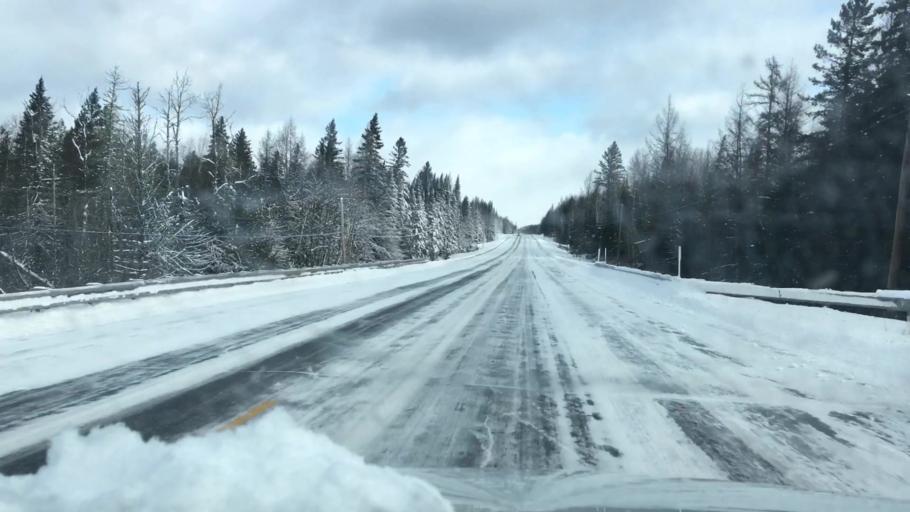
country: US
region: Maine
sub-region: Aroostook County
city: Madawaska
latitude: 47.0214
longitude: -68.0134
